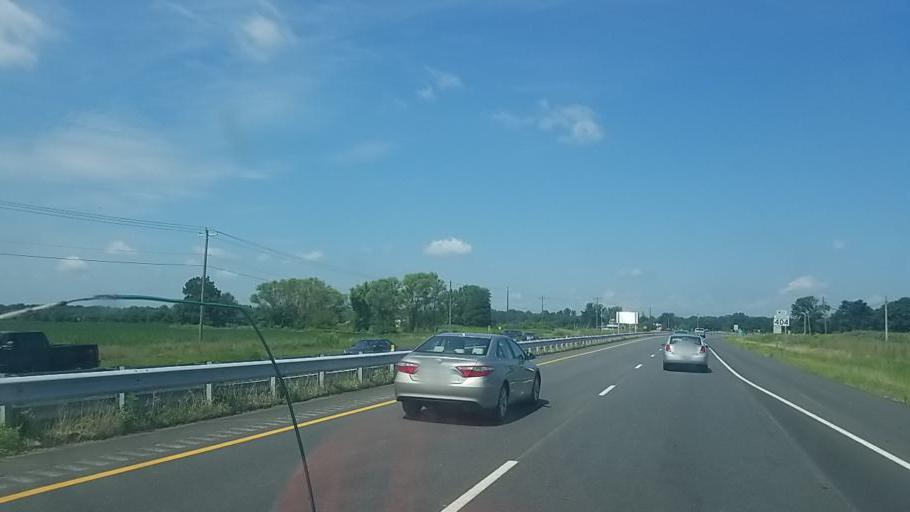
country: US
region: Maryland
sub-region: Caroline County
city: Ridgely
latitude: 38.9043
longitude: -75.8758
